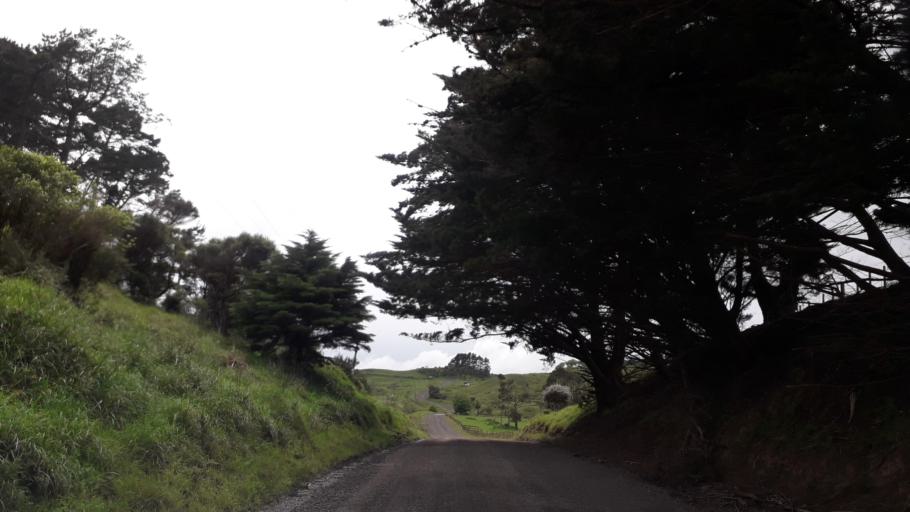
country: NZ
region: Northland
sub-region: Far North District
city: Ahipara
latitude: -35.4196
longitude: 173.3616
